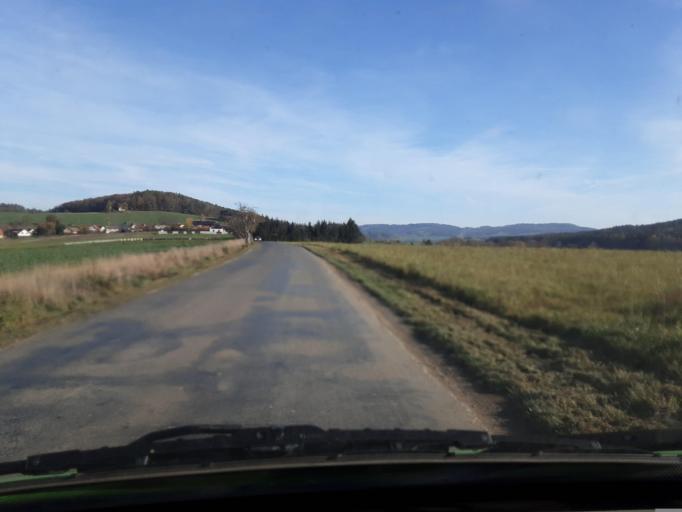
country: CZ
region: Plzensky
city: Klatovy
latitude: 49.3732
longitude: 13.3099
